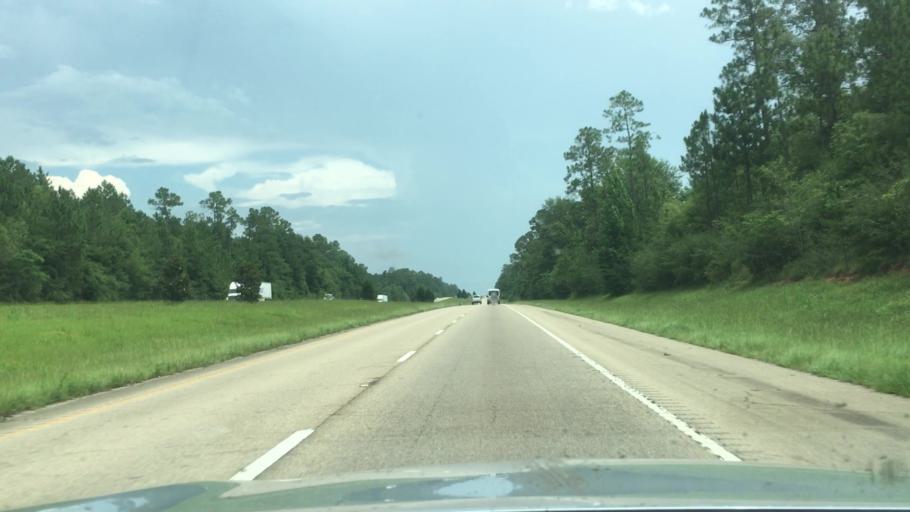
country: US
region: Mississippi
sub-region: Lamar County
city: Lumberton
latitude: 30.9486
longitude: -89.4451
